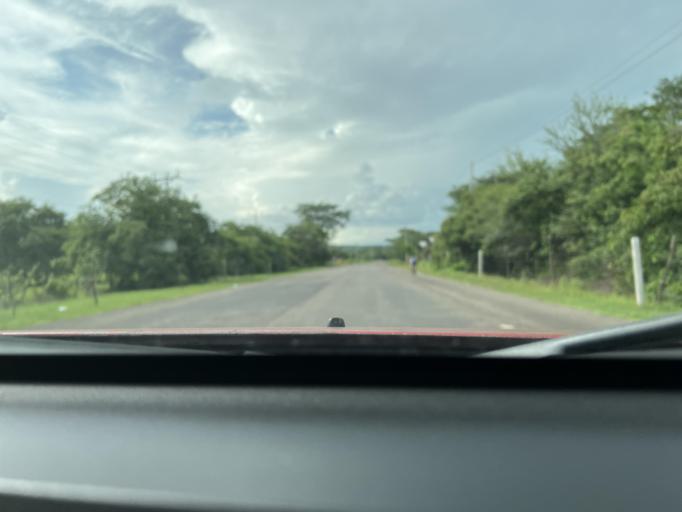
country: SV
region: La Union
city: La Union
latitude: 13.3754
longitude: -87.9089
